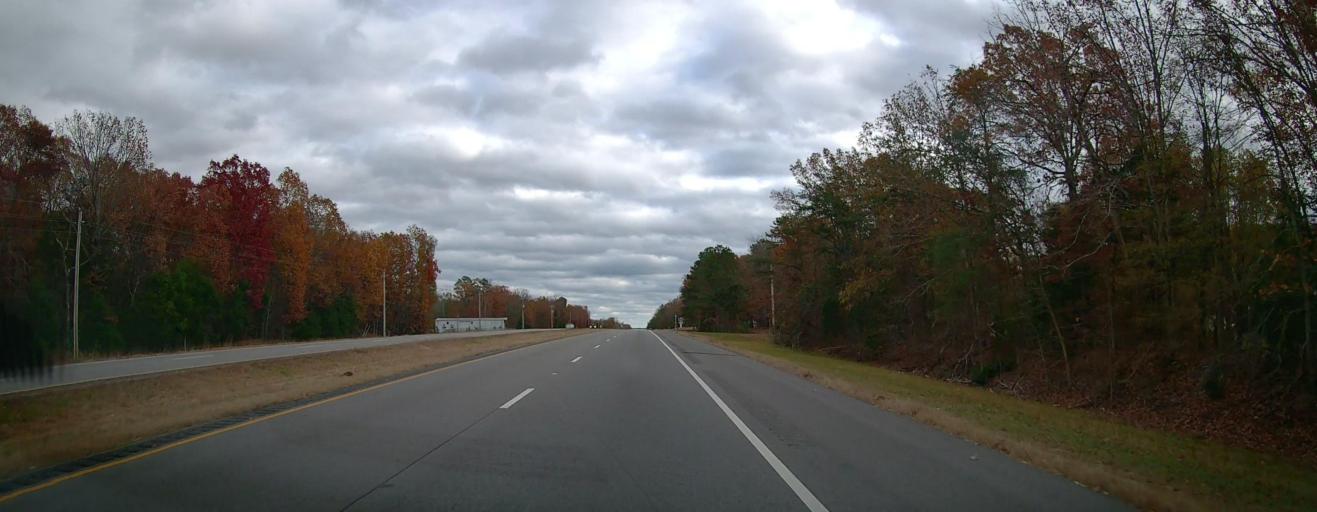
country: US
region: Alabama
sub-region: Colbert County
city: Muscle Shoals
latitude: 34.6686
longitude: -87.5584
